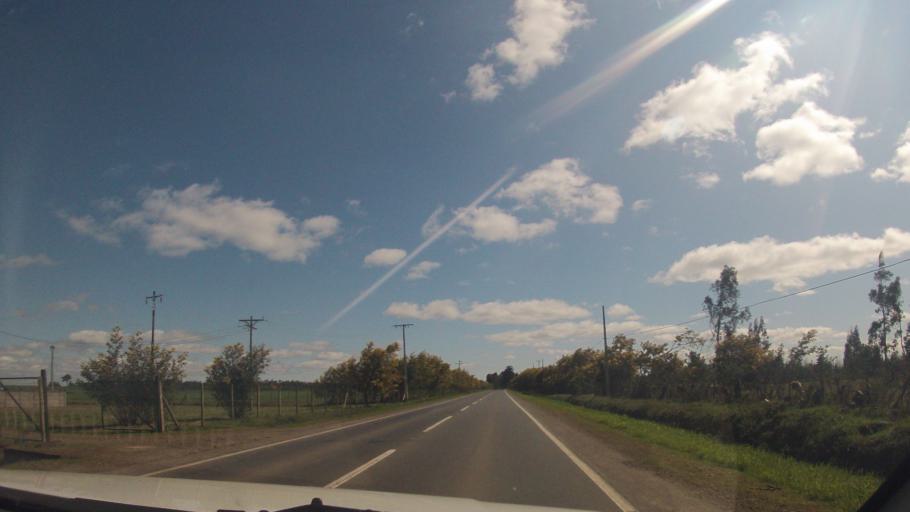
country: CL
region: Araucania
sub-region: Provincia de Malleco
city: Traiguen
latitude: -38.2618
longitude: -72.6161
